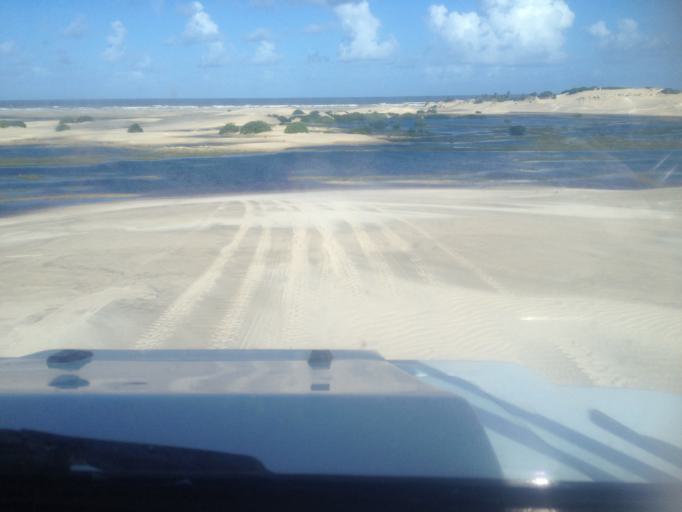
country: BR
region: Sergipe
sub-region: Indiaroba
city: Indiaroba
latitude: -11.4757
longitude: -37.3763
